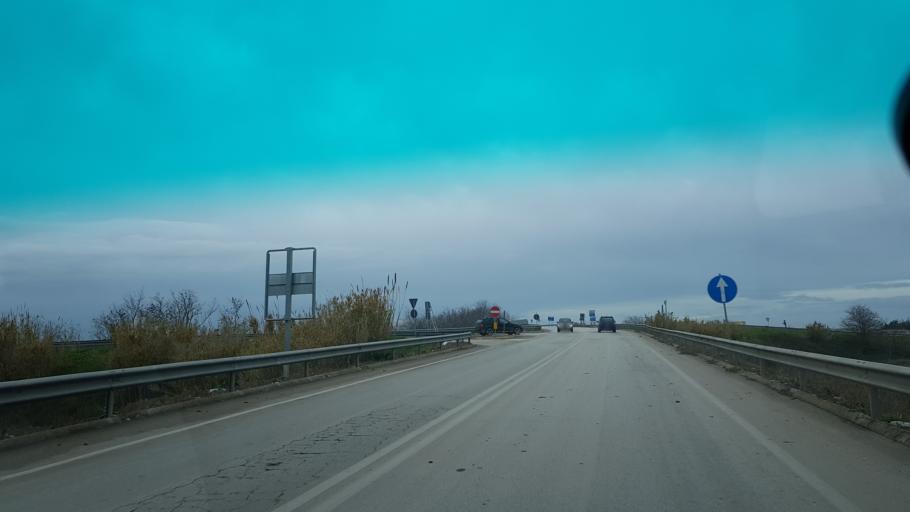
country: IT
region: Apulia
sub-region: Provincia di Brindisi
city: Mesagne
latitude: 40.5710
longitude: 17.8203
